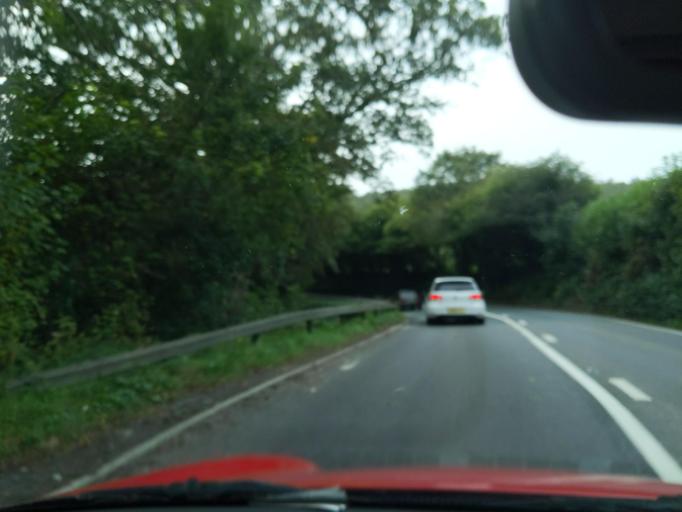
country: GB
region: England
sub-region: Devon
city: Horrabridge
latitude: 50.5153
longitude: -4.1149
